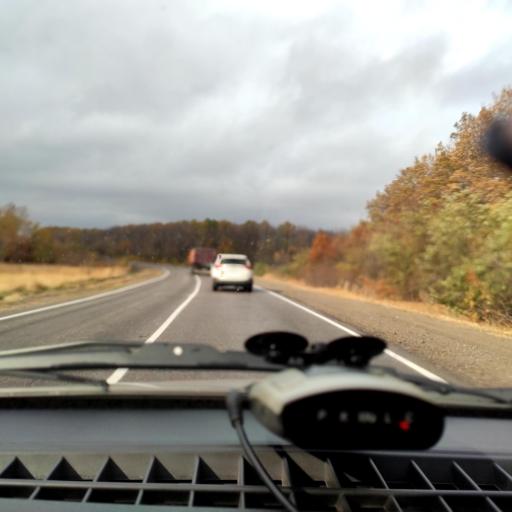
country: RU
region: Voronezj
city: Kolodeznyy
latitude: 51.3773
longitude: 39.0198
